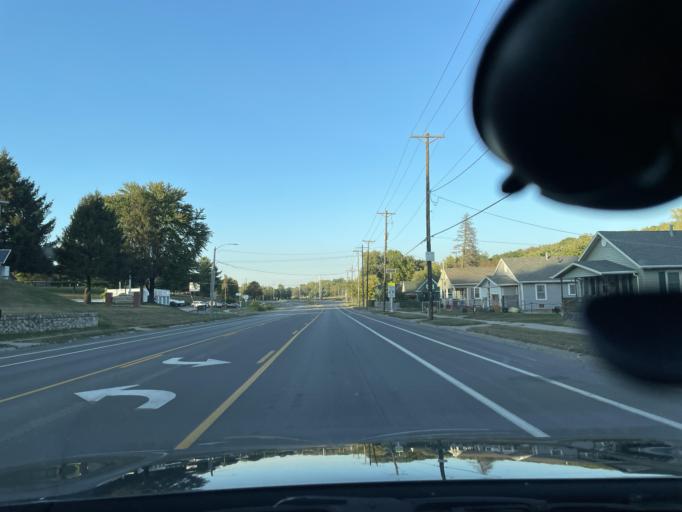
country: US
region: Missouri
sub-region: Buchanan County
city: Saint Joseph
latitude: 39.8020
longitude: -94.8431
